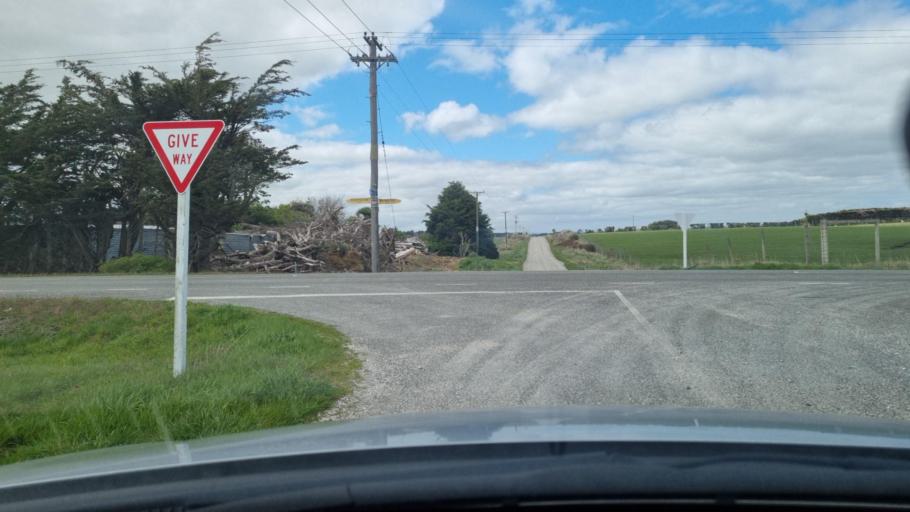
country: NZ
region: Southland
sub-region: Invercargill City
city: Invercargill
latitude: -46.4426
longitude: 168.4583
